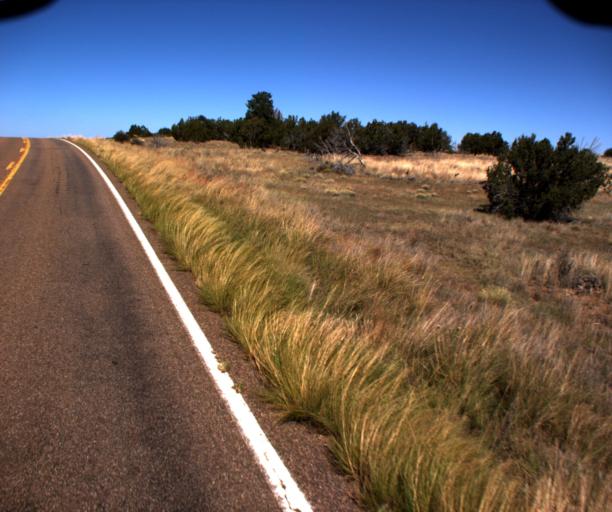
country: US
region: Arizona
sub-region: Navajo County
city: Heber-Overgaard
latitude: 34.4624
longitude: -110.4718
